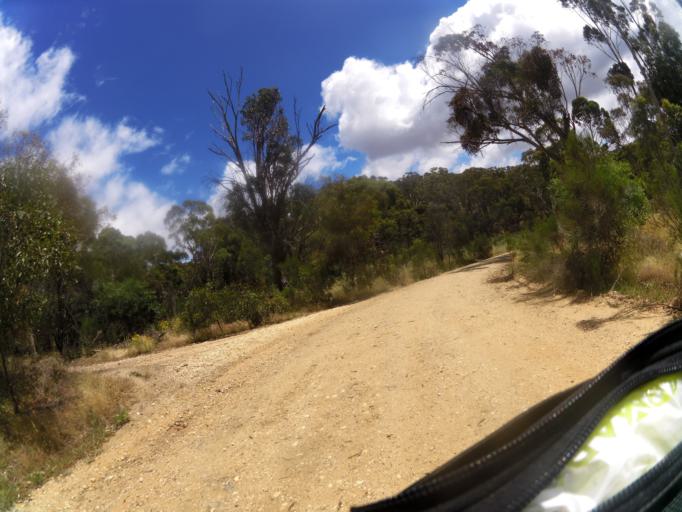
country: AU
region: Victoria
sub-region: Mount Alexander
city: Castlemaine
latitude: -37.0557
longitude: 144.2710
